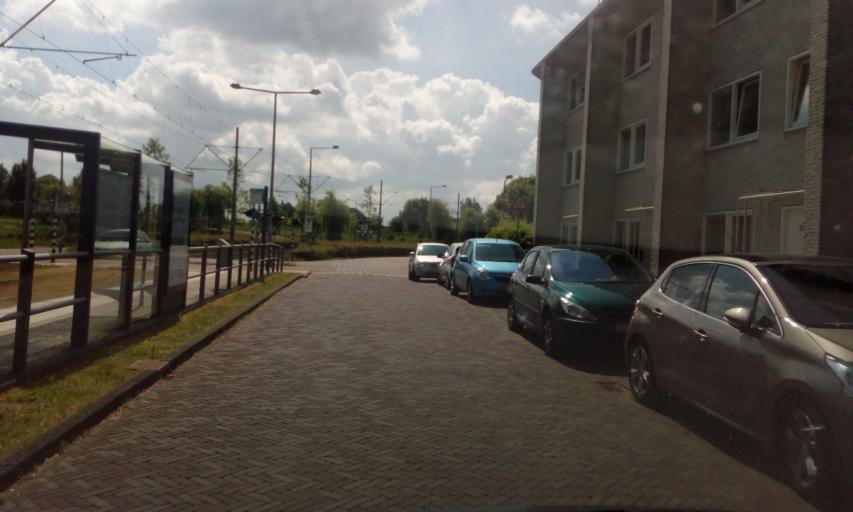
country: NL
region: South Holland
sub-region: Gemeente Den Haag
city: Ypenburg
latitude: 52.0689
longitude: 4.4052
